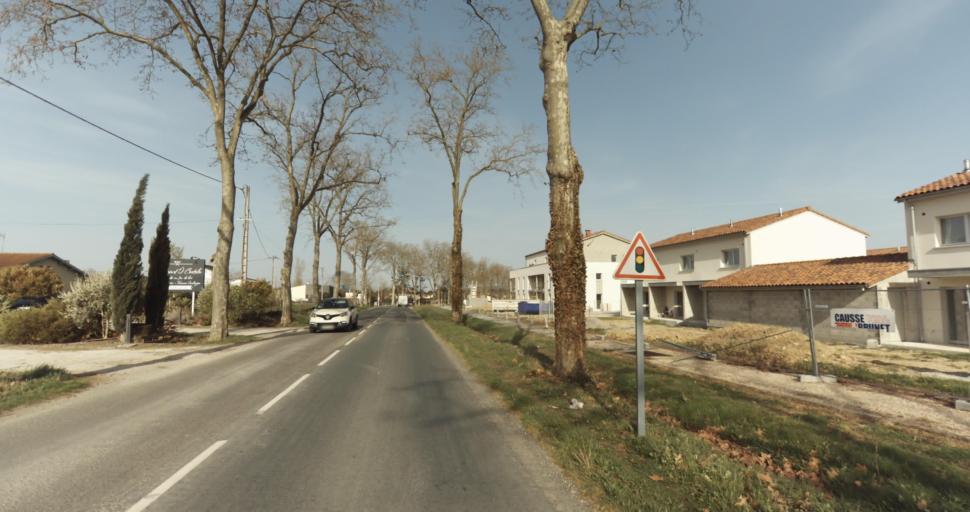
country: FR
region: Midi-Pyrenees
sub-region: Departement du Tarn
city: Saint-Sulpice-la-Pointe
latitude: 43.7611
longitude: 1.6999
